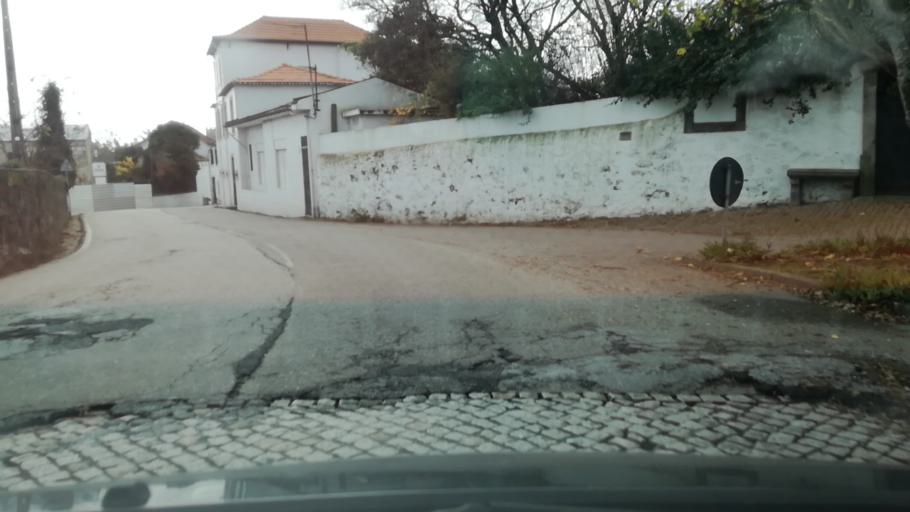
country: PT
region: Porto
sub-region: Maia
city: Maia
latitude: 41.2471
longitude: -8.6364
